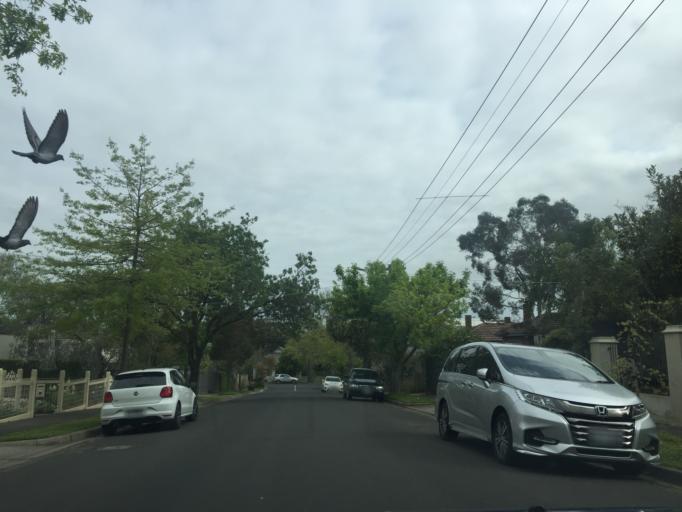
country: AU
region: Victoria
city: Balwyn
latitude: -37.8180
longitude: 145.0558
